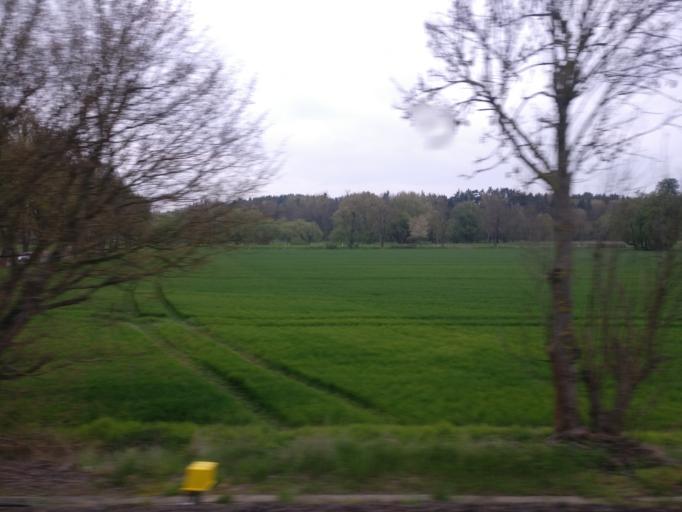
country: DE
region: Lower Saxony
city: Holle
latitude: 52.1000
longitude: 10.1248
